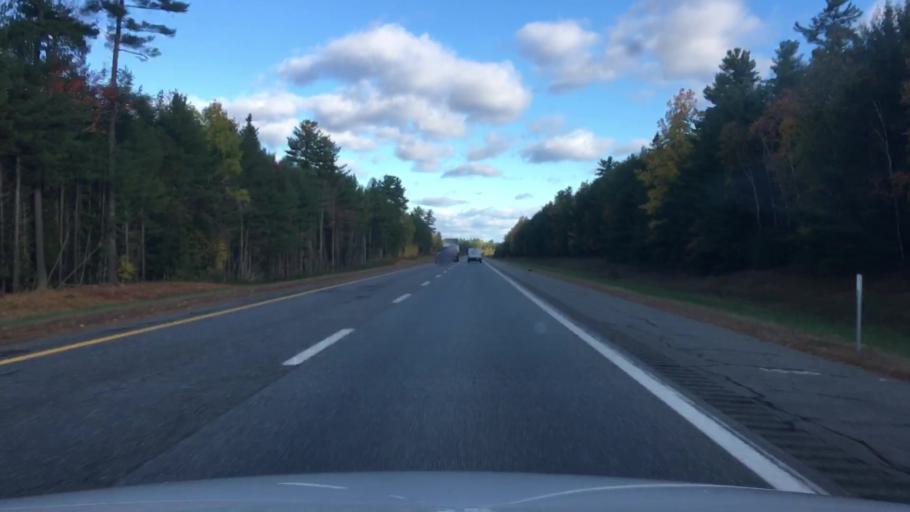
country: US
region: Maine
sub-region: Penobscot County
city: Greenbush
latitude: 45.1395
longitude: -68.7000
